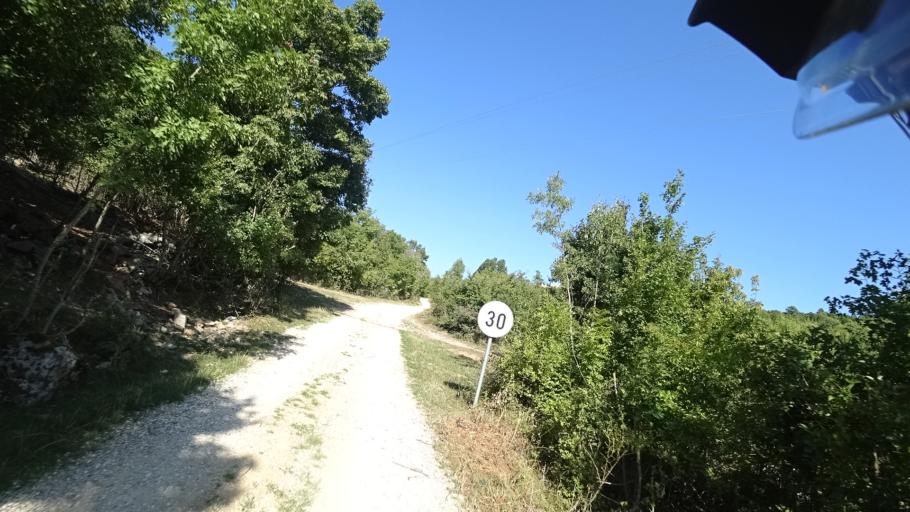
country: HR
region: Zadarska
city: Gracac
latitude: 44.2989
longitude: 16.0303
